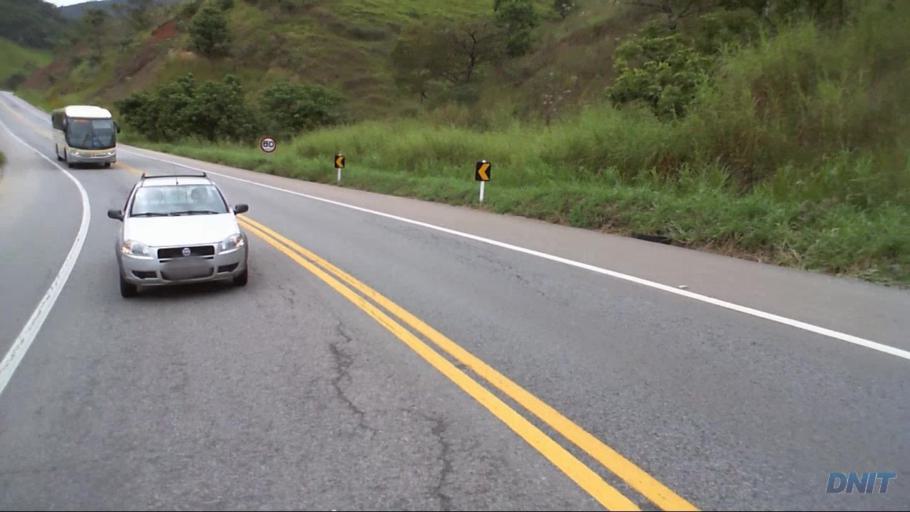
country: BR
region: Minas Gerais
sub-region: Timoteo
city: Timoteo
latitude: -19.6200
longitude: -42.8454
